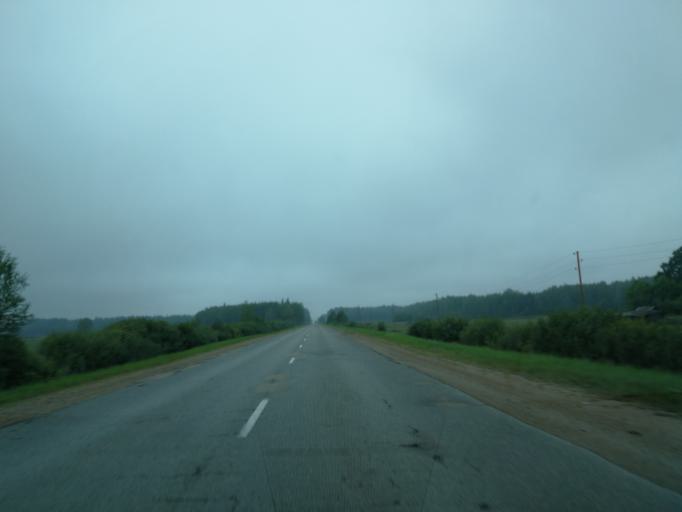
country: LV
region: Varkava
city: Vecvarkava
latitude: 56.3185
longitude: 26.4577
